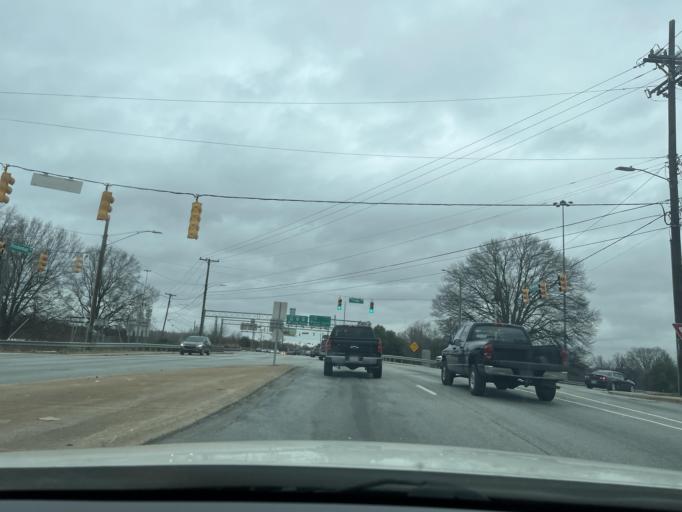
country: US
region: North Carolina
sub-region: Guilford County
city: Greensboro
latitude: 36.0323
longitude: -79.8009
